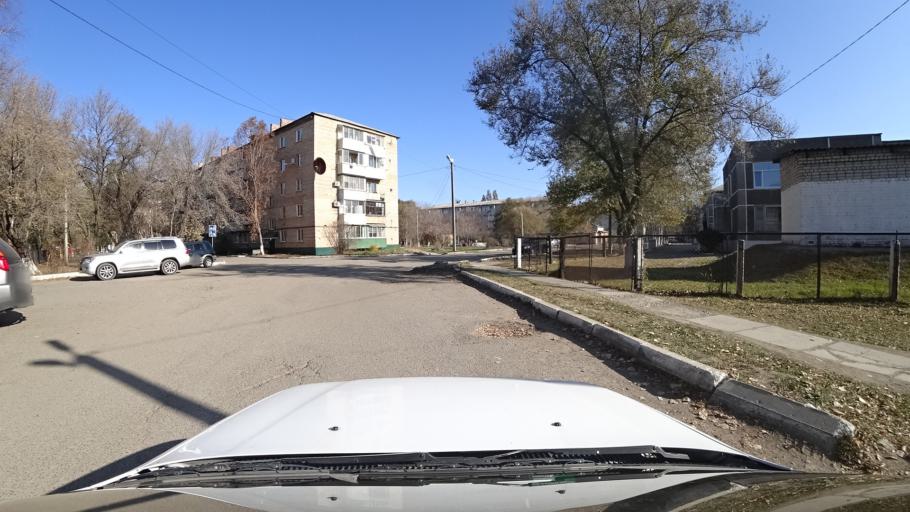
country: RU
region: Primorskiy
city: Dal'nerechensk
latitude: 45.9342
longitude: 133.7322
